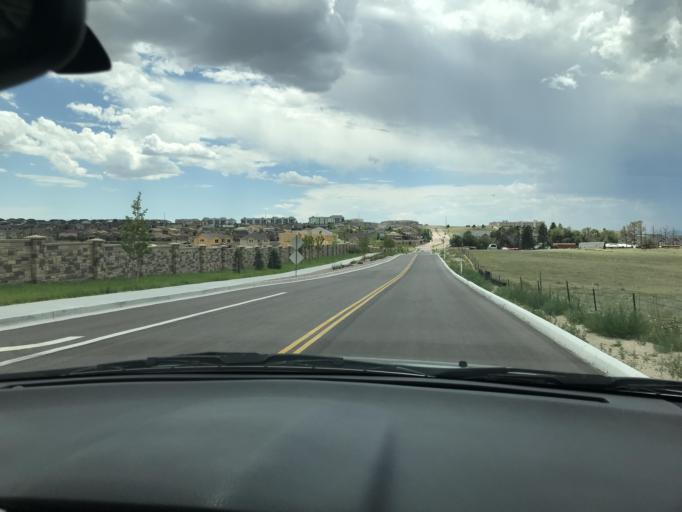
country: US
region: Colorado
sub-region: El Paso County
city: Black Forest
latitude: 38.9546
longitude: -104.7144
